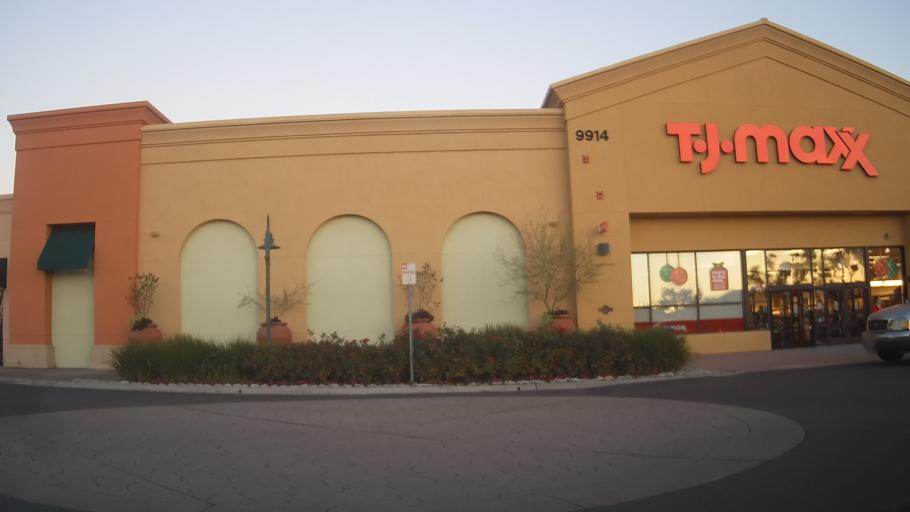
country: US
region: California
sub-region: San Diego County
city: Santee
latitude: 32.8406
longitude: -116.9806
